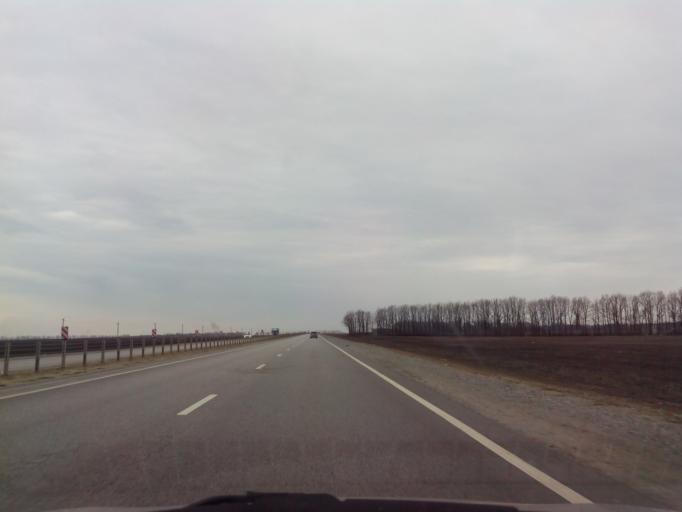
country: RU
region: Tambov
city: Zavoronezhskoye
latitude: 52.9015
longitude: 40.6587
